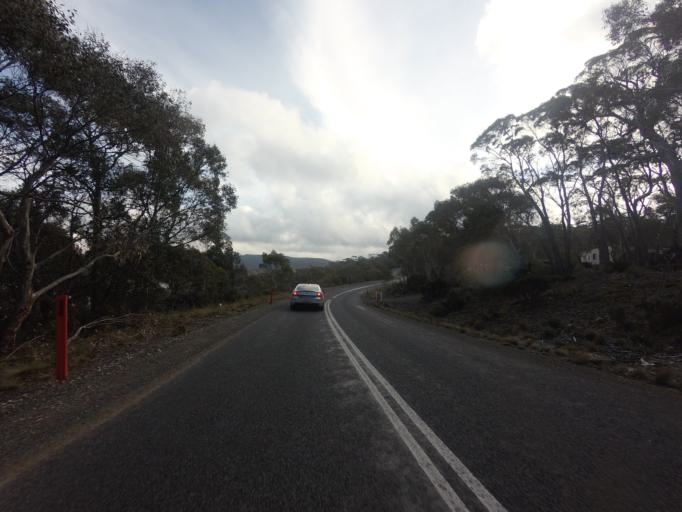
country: AU
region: Tasmania
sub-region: Meander Valley
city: Deloraine
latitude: -41.7923
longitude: 146.6923
